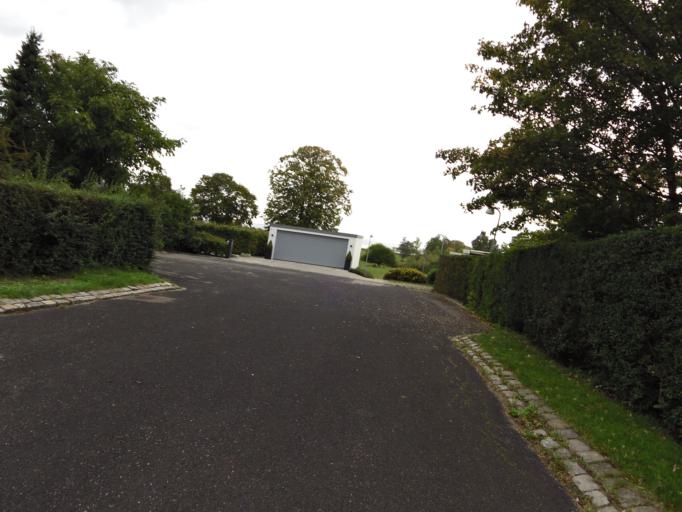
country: DK
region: Capital Region
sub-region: Fredensborg Kommune
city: Niva
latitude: 55.9370
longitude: 12.5164
